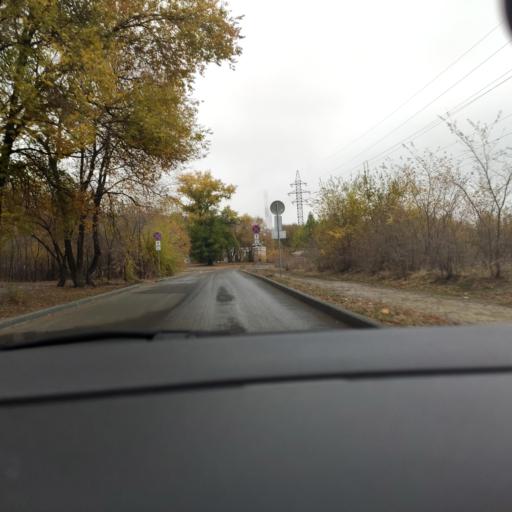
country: RU
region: Voronezj
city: Voronezh
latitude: 51.6355
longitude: 39.2310
